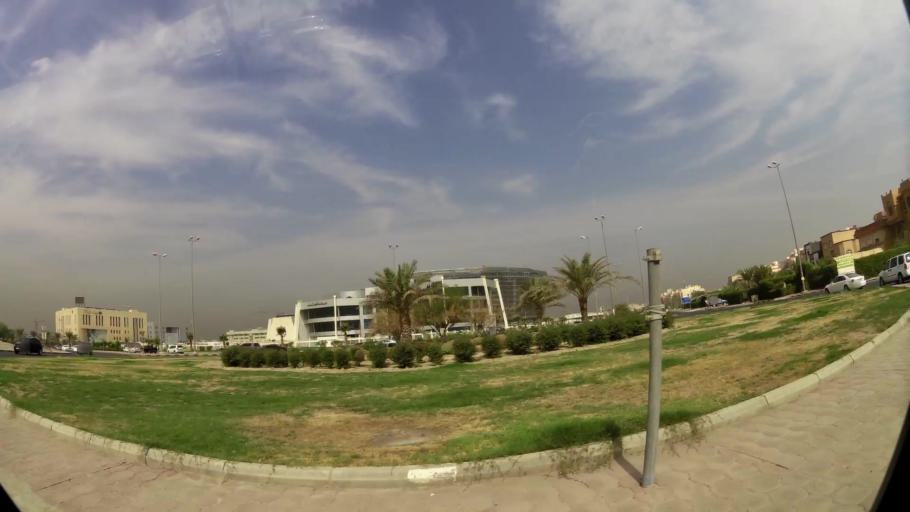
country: KW
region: Mubarak al Kabir
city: Sabah as Salim
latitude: 29.2685
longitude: 48.0224
